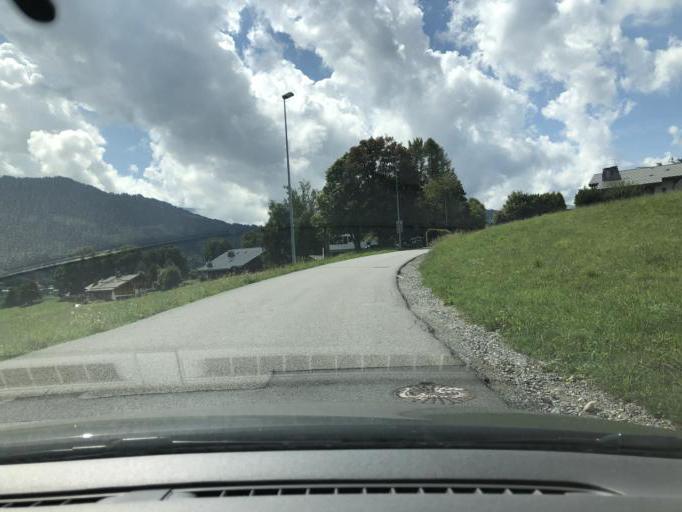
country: FR
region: Rhone-Alpes
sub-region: Departement de la Haute-Savoie
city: Combloux
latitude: 45.8893
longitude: 6.6367
